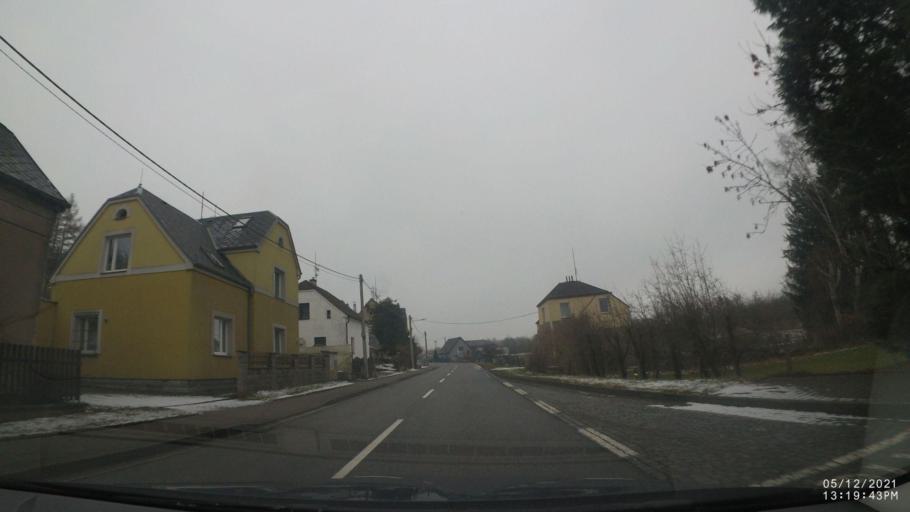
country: CZ
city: Velke Porici
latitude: 50.4444
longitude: 16.1912
